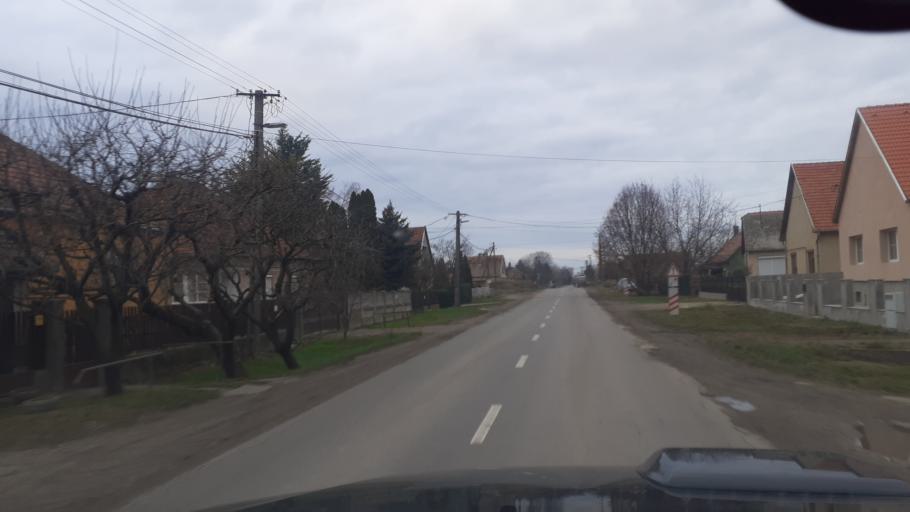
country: HU
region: Bacs-Kiskun
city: Szalkszentmarton
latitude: 46.9692
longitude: 19.0233
